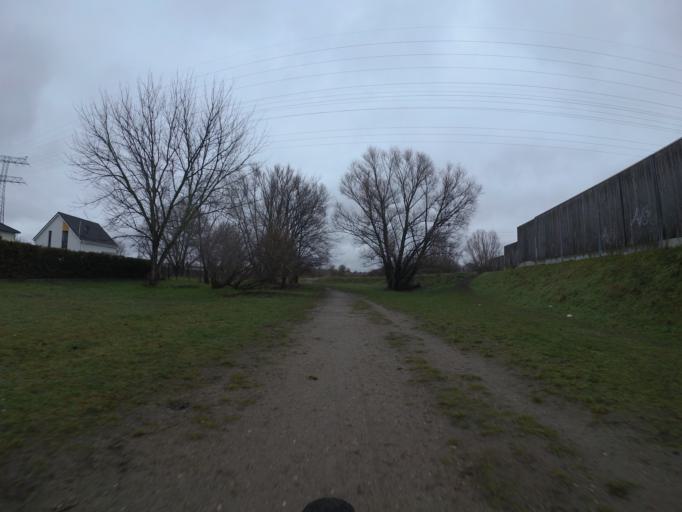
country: DE
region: Berlin
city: Hellersdorf
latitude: 52.5516
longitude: 13.5947
